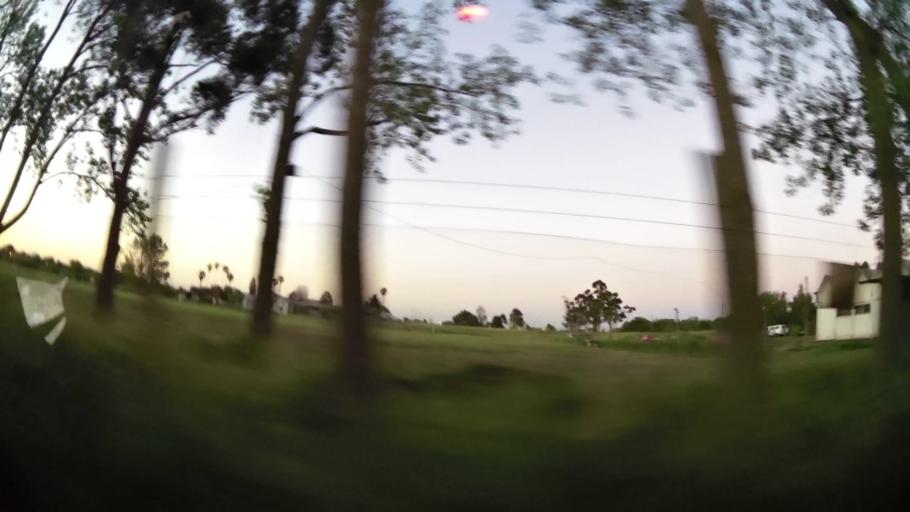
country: UY
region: Montevideo
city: Montevideo
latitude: -34.8214
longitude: -56.1461
